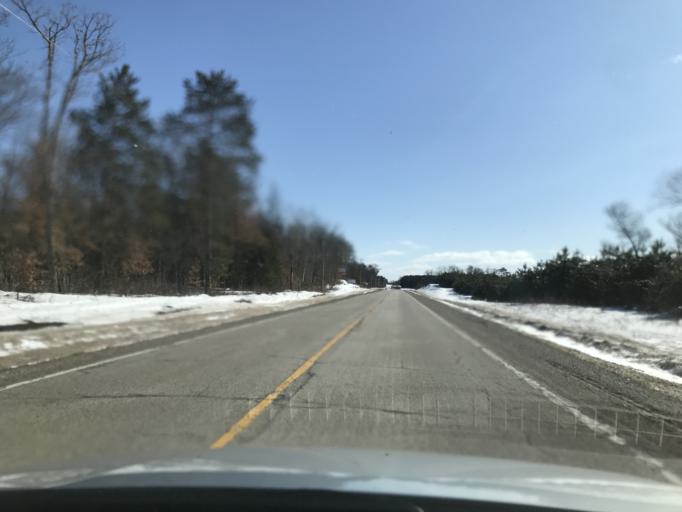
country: US
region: Wisconsin
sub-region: Marinette County
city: Niagara
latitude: 45.3549
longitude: -88.1012
